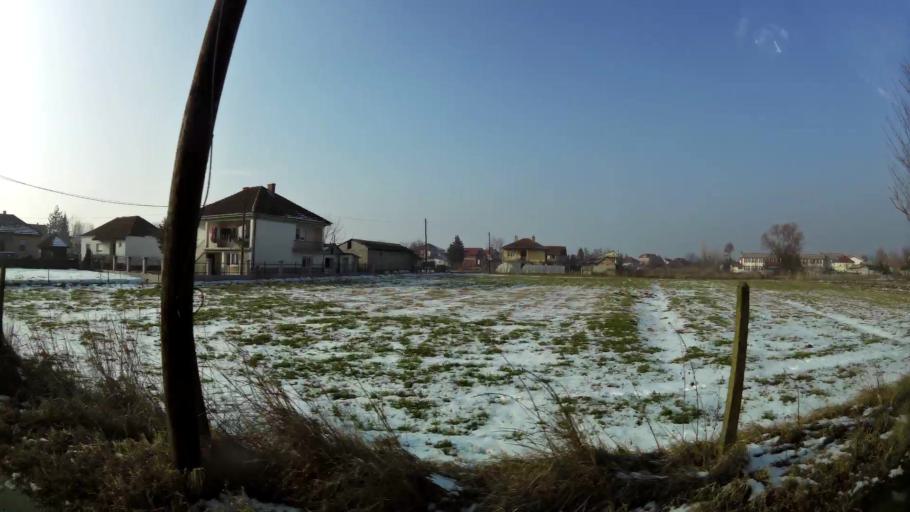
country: MK
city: Kadino
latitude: 41.9669
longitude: 21.5953
